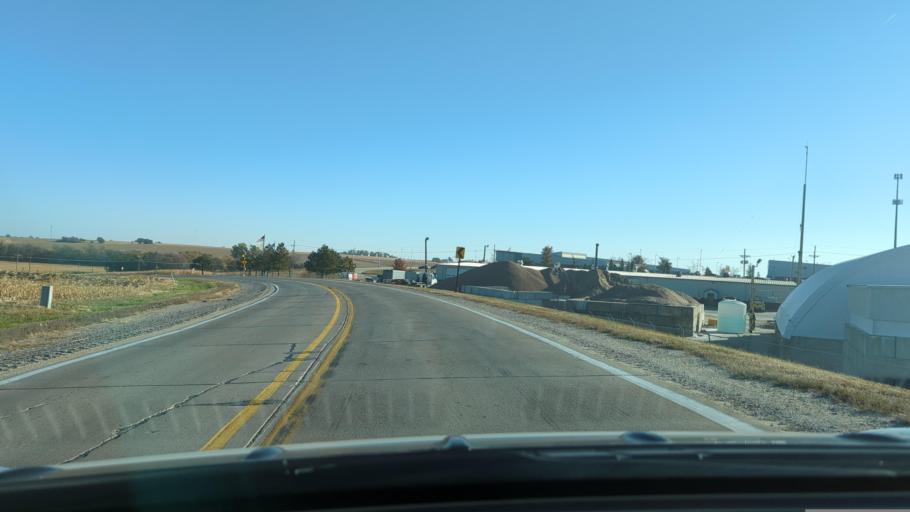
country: US
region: Nebraska
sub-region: Sarpy County
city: Papillion
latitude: 41.0889
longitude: -96.0453
